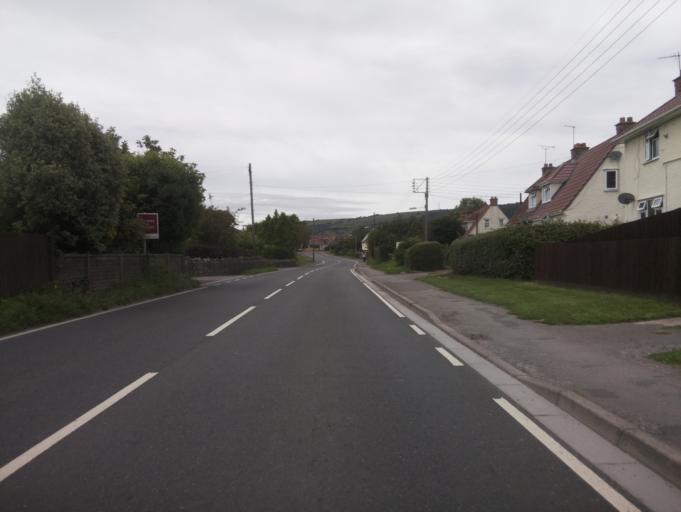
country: GB
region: England
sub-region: Somerset
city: Cheddar
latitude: 51.2770
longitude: -2.7853
